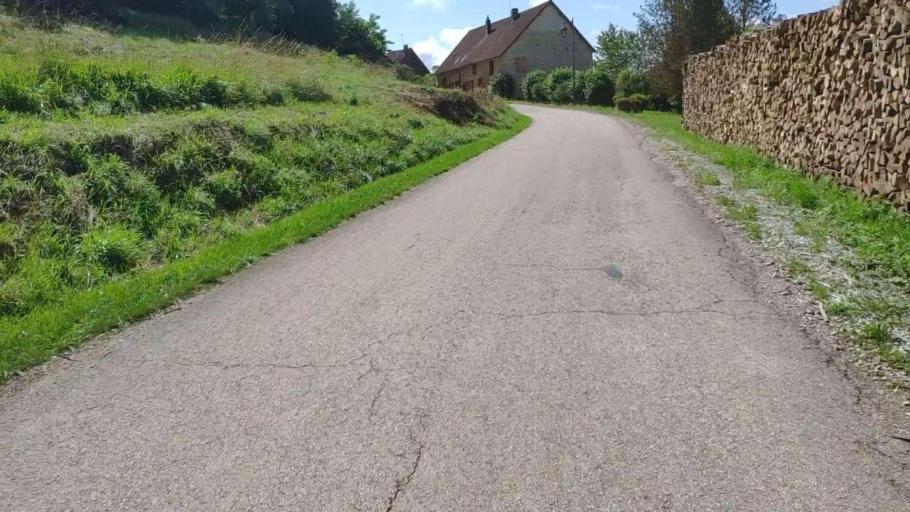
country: FR
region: Franche-Comte
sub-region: Departement du Jura
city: Bletterans
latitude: 46.8033
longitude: 5.5572
